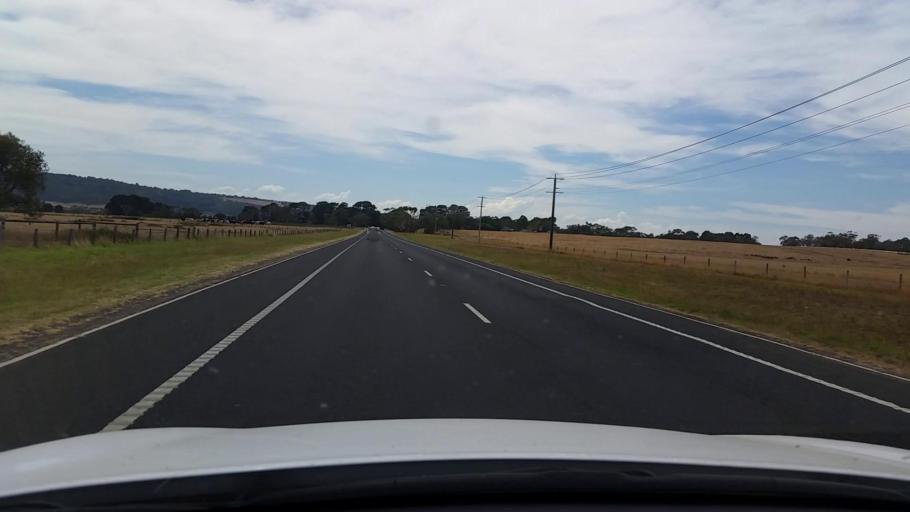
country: AU
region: Victoria
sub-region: Mornington Peninsula
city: Safety Beach
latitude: -38.3267
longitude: 145.0121
